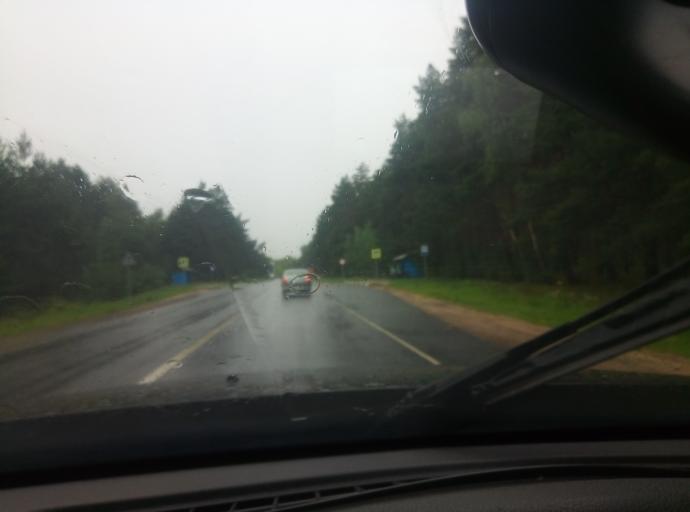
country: RU
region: Moskovskaya
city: Protvino
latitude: 54.8766
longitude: 37.2502
